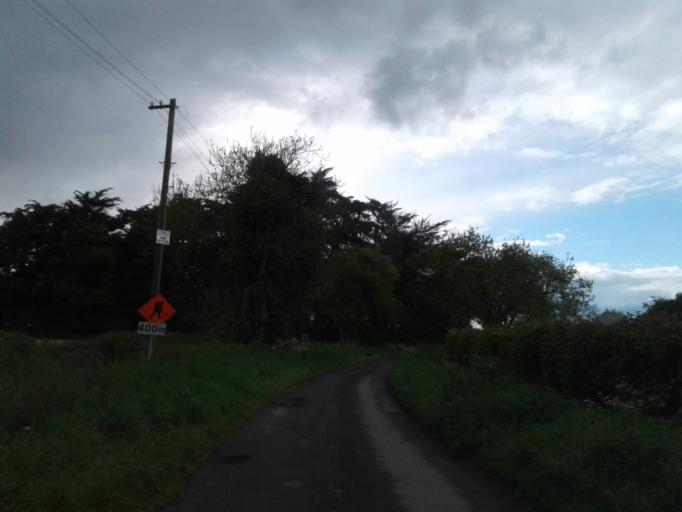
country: IE
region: Leinster
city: Ballymun
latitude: 53.4313
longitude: -6.2887
